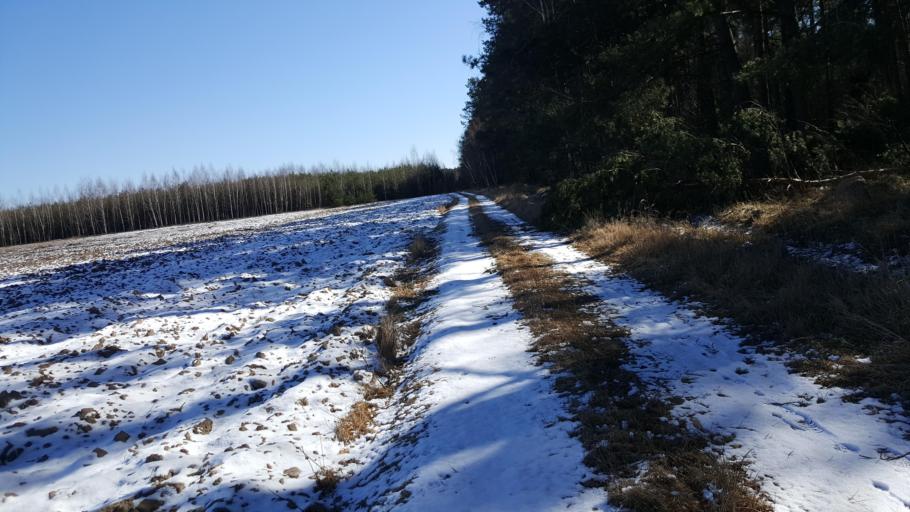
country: BY
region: Brest
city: Kamyanyets
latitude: 52.3708
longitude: 23.8118
